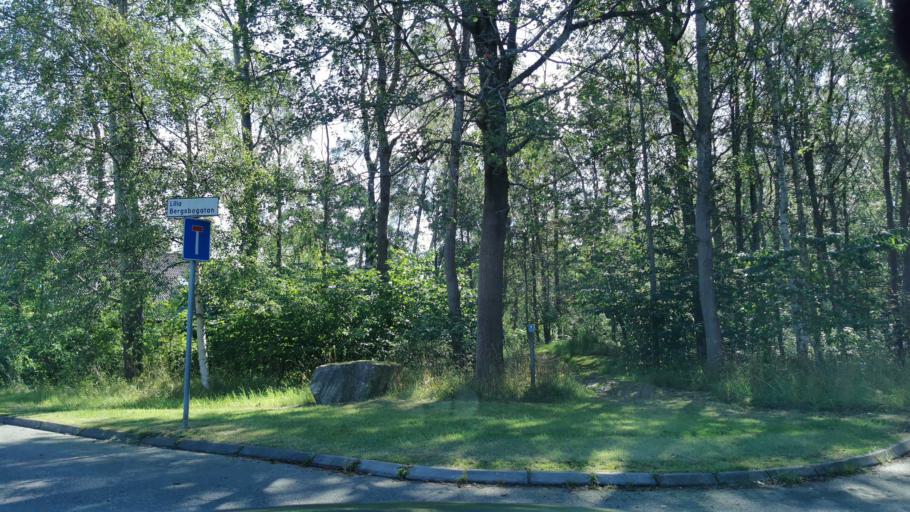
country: SE
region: Vaestra Goetaland
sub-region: Molndal
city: Moelndal
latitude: 57.6728
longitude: 11.9902
